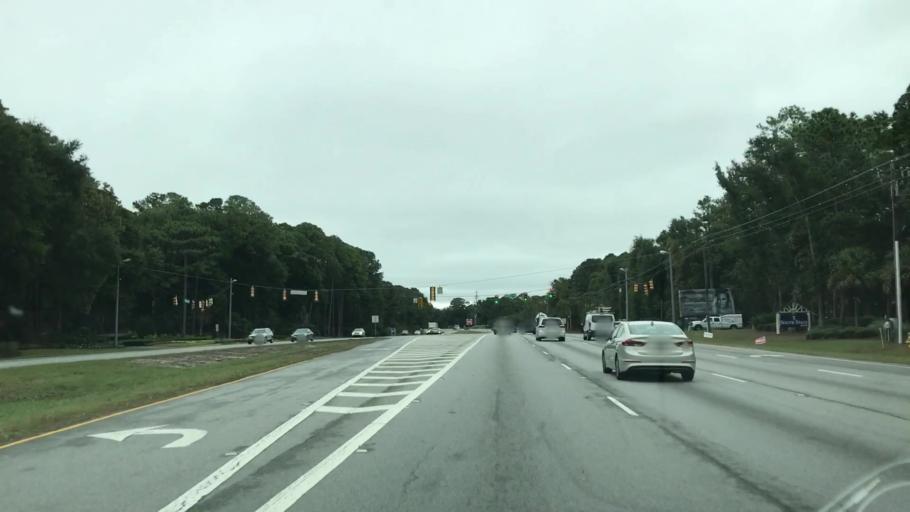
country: US
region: South Carolina
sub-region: Beaufort County
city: Bluffton
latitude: 32.2445
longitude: -80.8272
